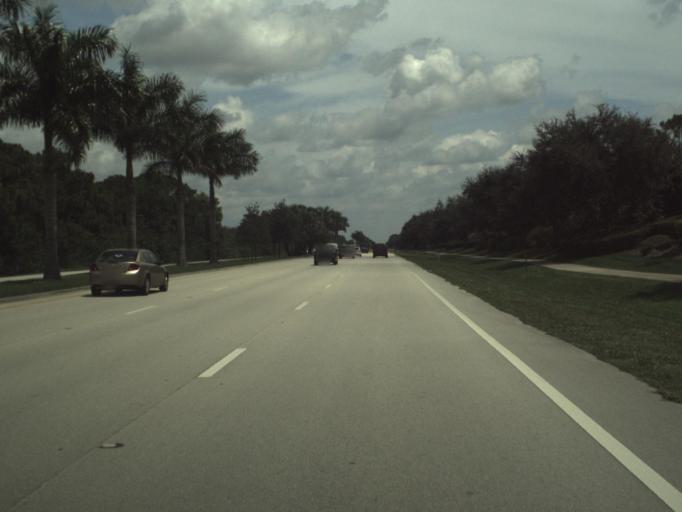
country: US
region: Florida
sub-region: Palm Beach County
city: Juno Beach
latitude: 26.8868
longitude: -80.0950
